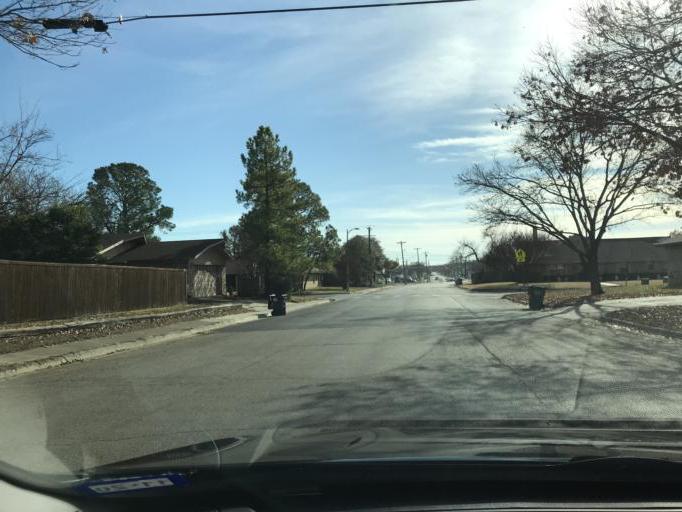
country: US
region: Texas
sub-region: Denton County
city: Denton
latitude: 33.2319
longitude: -97.1495
